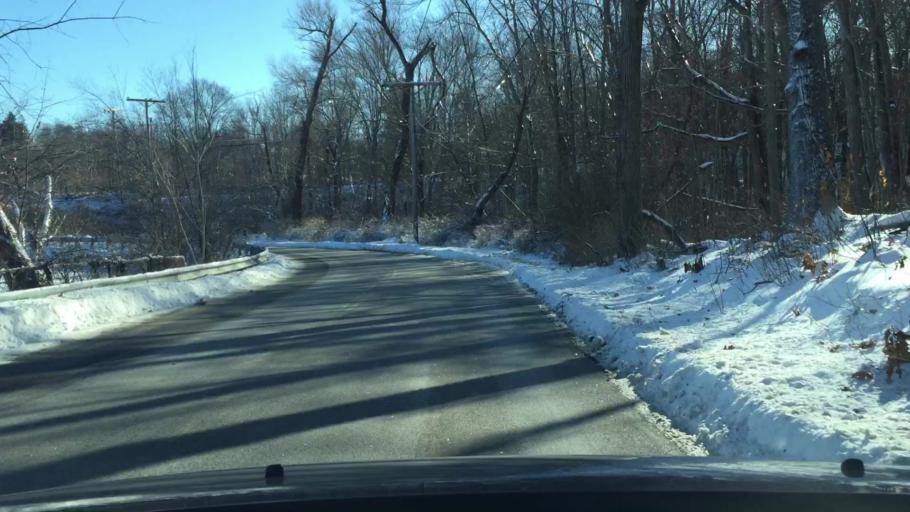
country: US
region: Massachusetts
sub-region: Essex County
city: North Andover
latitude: 42.6871
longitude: -71.1036
